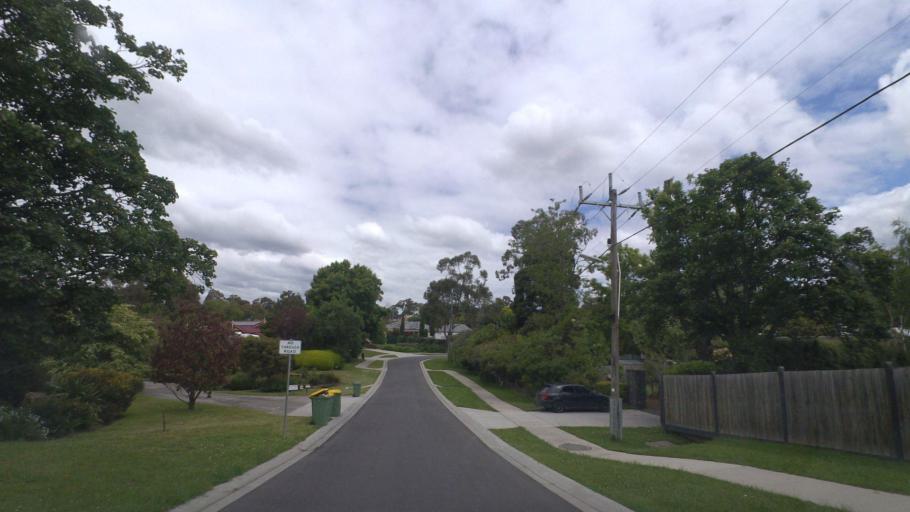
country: AU
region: Victoria
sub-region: Yarra Ranges
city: Mount Evelyn
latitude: -37.7790
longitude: 145.4294
